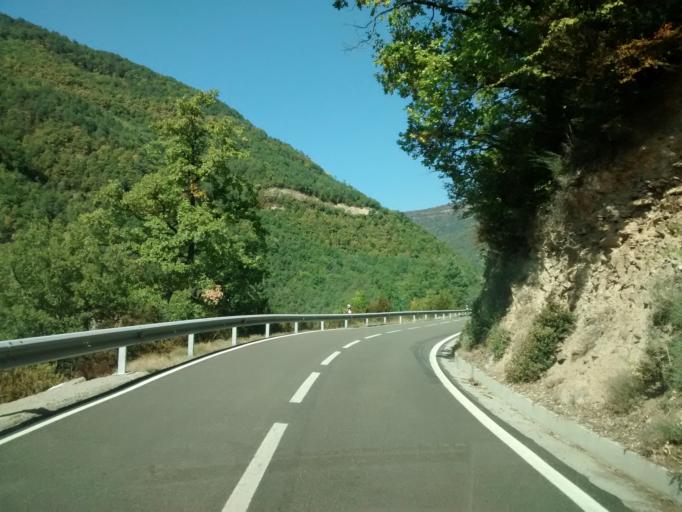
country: ES
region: Aragon
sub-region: Provincia de Huesca
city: Fiscal
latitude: 42.5235
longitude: -0.1329
